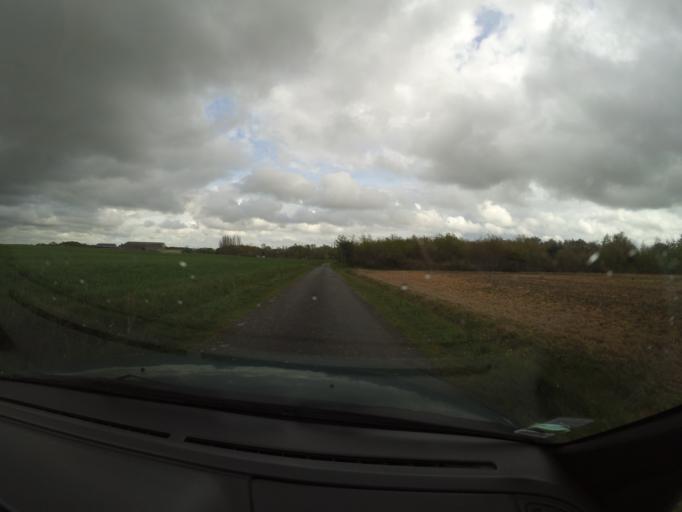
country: FR
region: Pays de la Loire
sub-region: Departement de la Loire-Atlantique
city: Remouille
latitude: 47.0720
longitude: -1.3620
